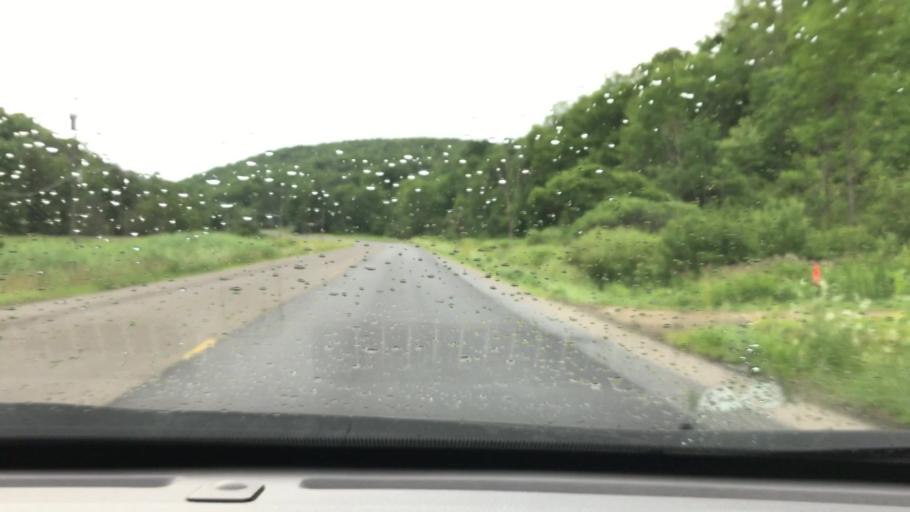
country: US
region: New York
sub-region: Cattaraugus County
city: Salamanca
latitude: 42.2937
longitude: -78.6632
